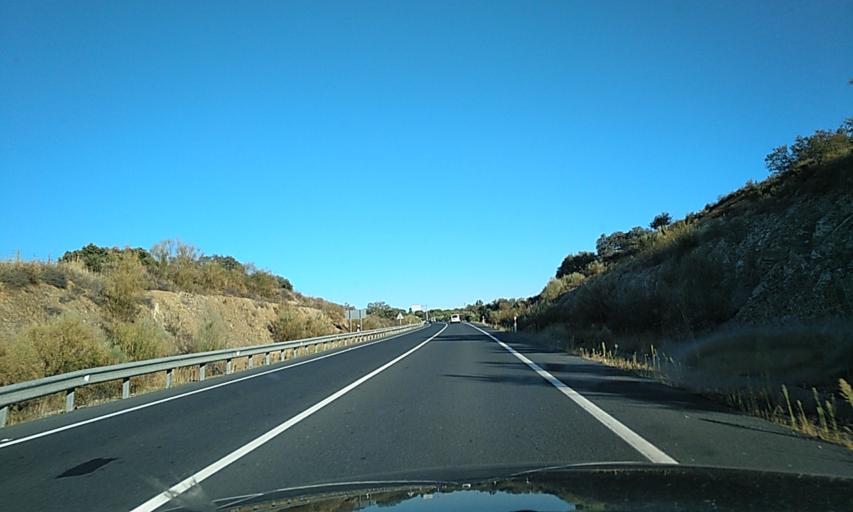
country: ES
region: Andalusia
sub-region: Provincia de Huelva
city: San Bartolome de la Torre
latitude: 37.4361
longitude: -7.1147
